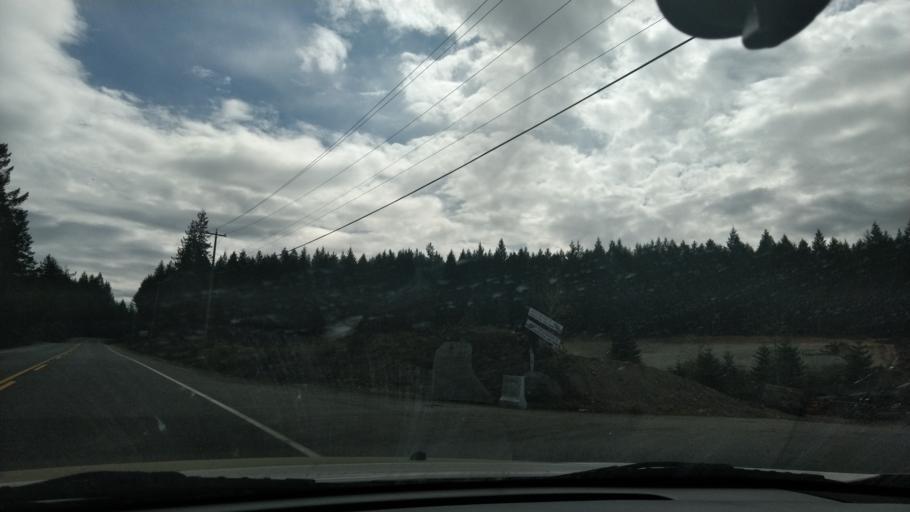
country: CA
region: British Columbia
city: Campbell River
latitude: 50.0232
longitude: -125.3533
